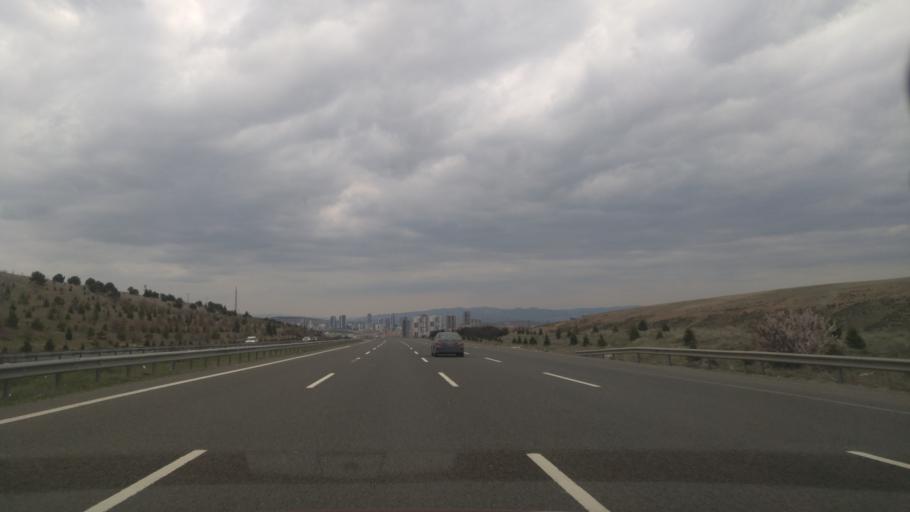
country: TR
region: Ankara
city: Etimesgut
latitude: 39.8149
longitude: 32.6454
